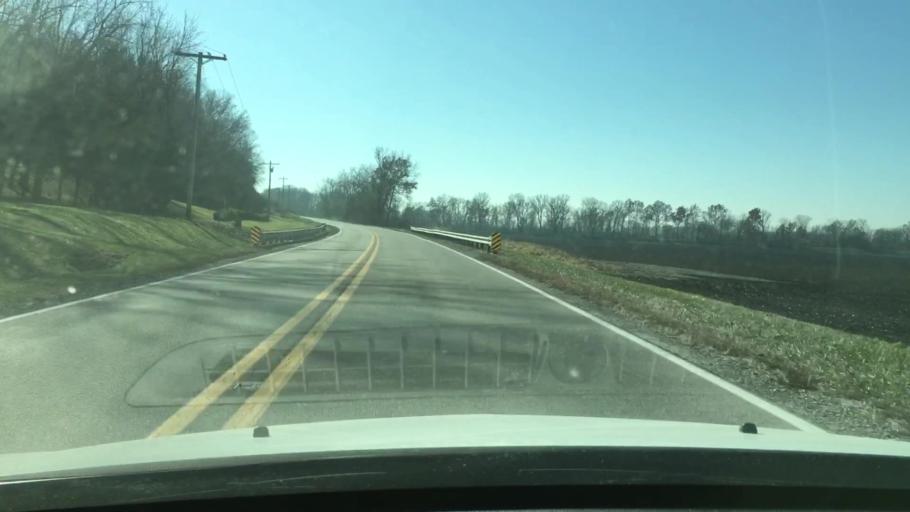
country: US
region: Illinois
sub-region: Morgan County
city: Meredosia
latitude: 39.7234
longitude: -90.5682
